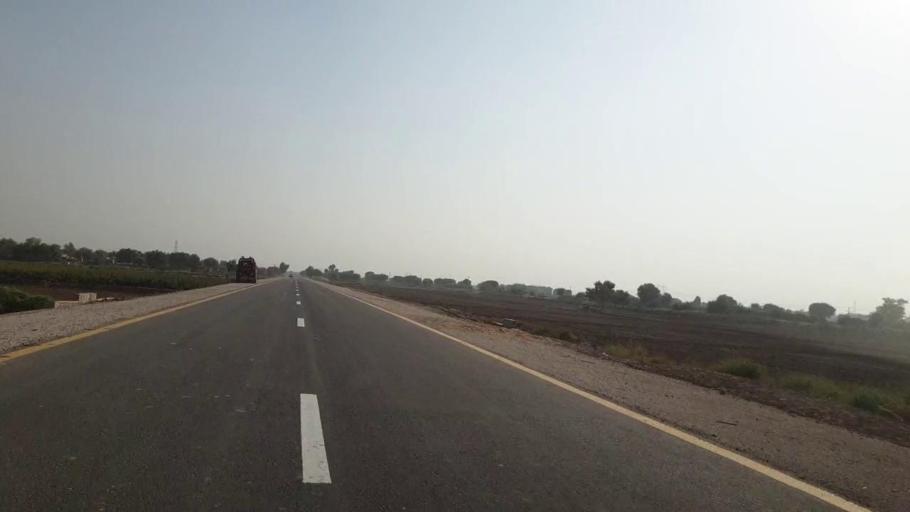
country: PK
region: Sindh
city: Bhan
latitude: 26.4927
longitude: 67.7799
